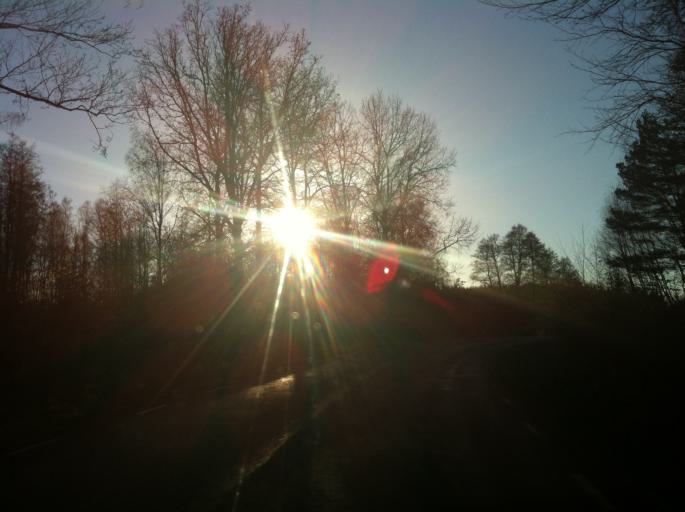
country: SE
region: Blekinge
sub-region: Olofstroms Kommun
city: Jamshog
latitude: 56.1857
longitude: 14.5872
